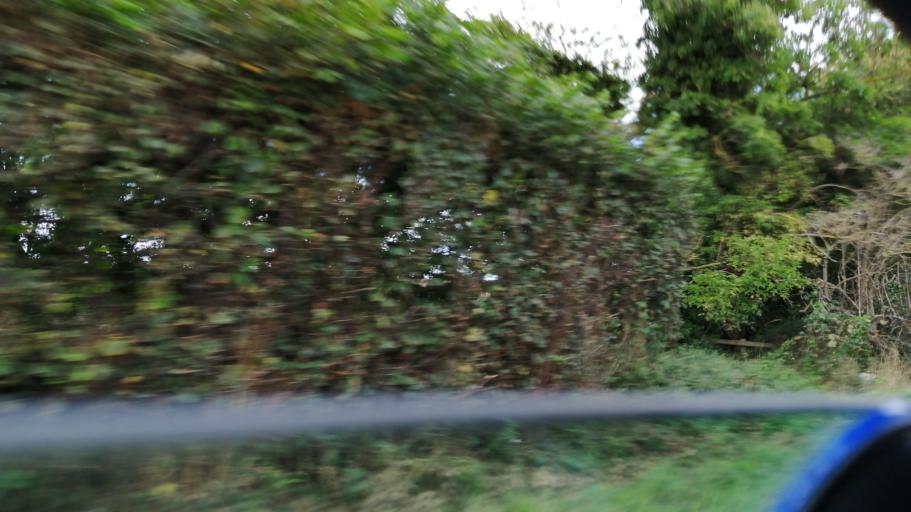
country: GB
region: England
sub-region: Herefordshire
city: Callow
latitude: 52.0193
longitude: -2.7286
